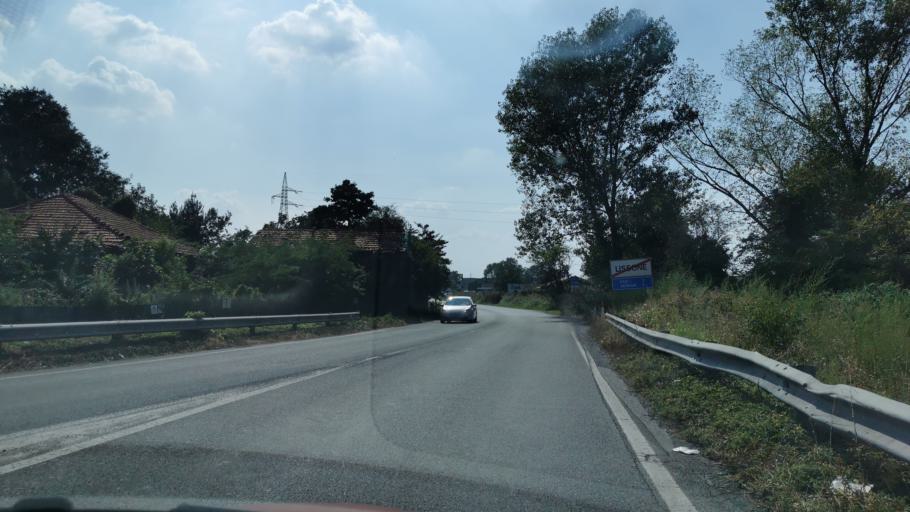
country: IT
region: Lombardy
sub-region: Provincia di Monza e Brianza
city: Muggio
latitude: 45.6056
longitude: 9.2233
